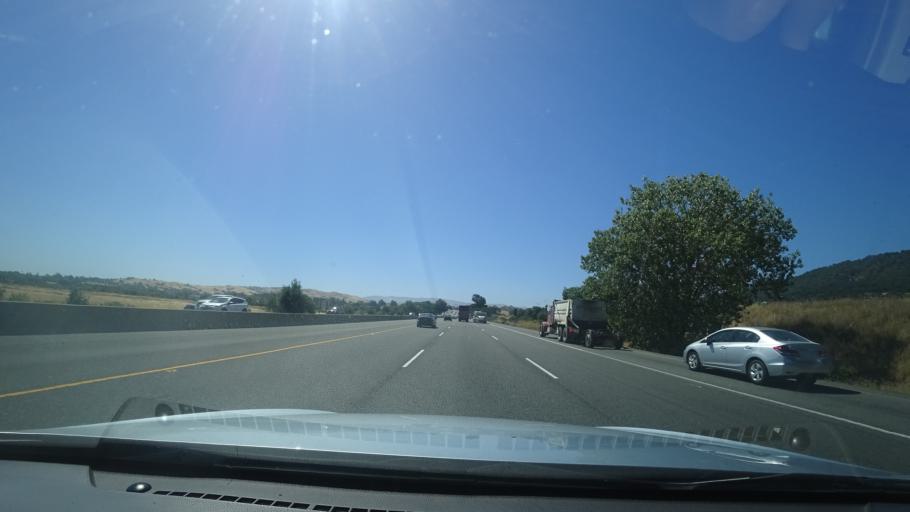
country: US
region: California
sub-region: Alameda County
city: Pleasanton
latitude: 37.6519
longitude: -121.8966
